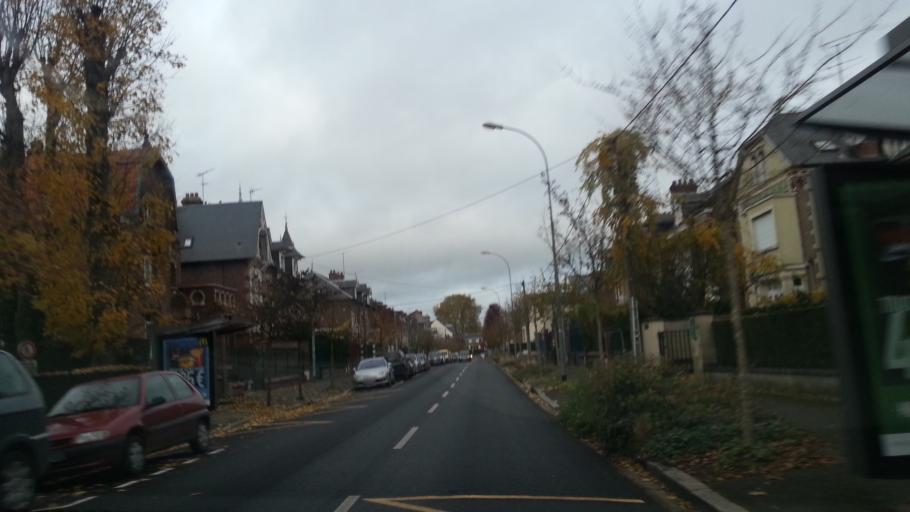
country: FR
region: Picardie
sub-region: Departement de l'Oise
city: Beauvais
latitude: 49.4349
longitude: 2.0785
